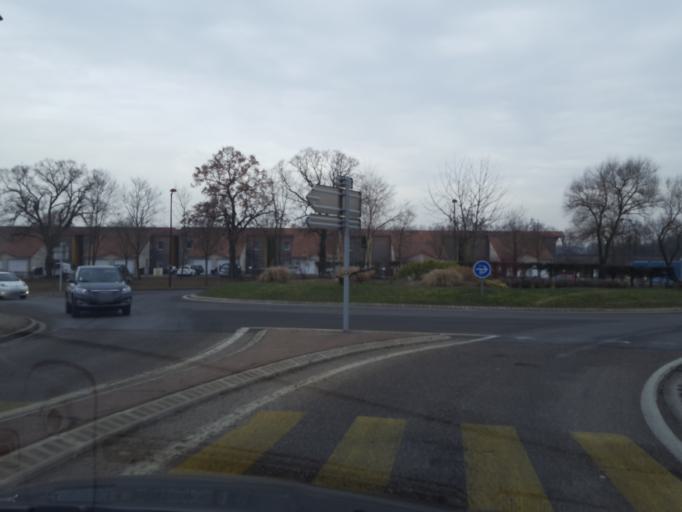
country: FR
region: Lorraine
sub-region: Departement de la Moselle
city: Moulins-les-Metz
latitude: 49.0910
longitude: 6.1219
